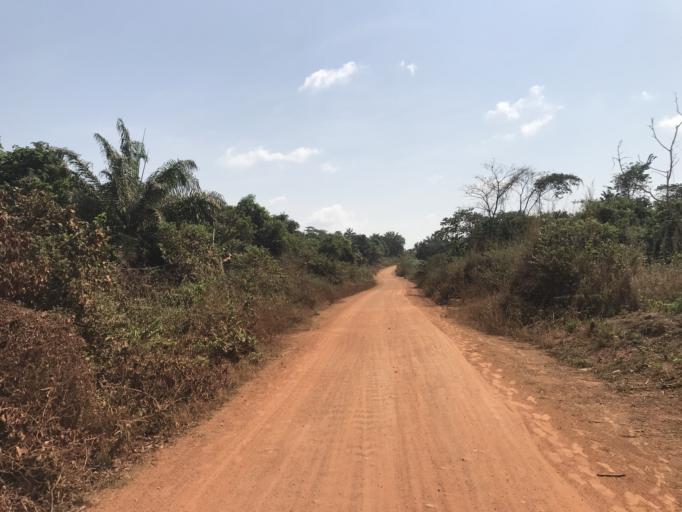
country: NG
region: Osun
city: Ifon
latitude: 7.8943
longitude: 4.4764
